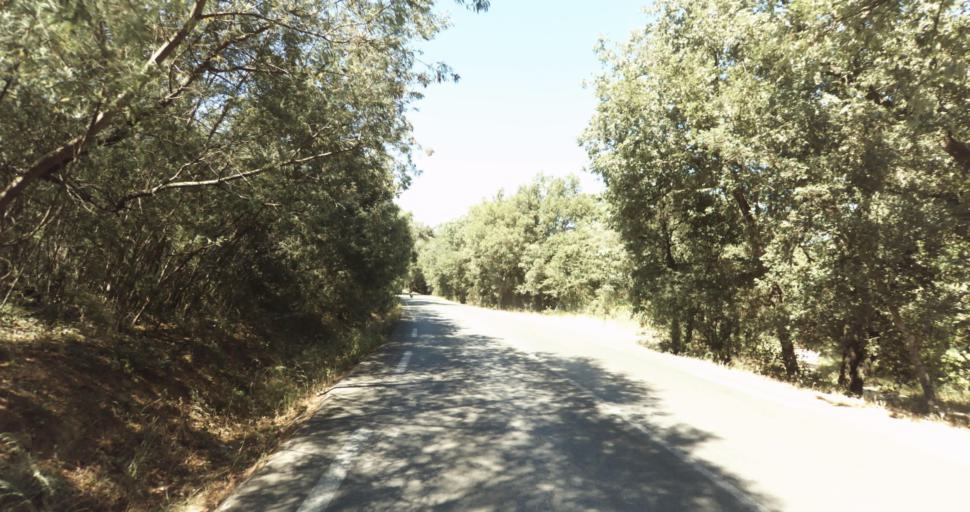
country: FR
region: Provence-Alpes-Cote d'Azur
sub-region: Departement du Var
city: La Croix-Valmer
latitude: 43.2189
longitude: 6.5698
